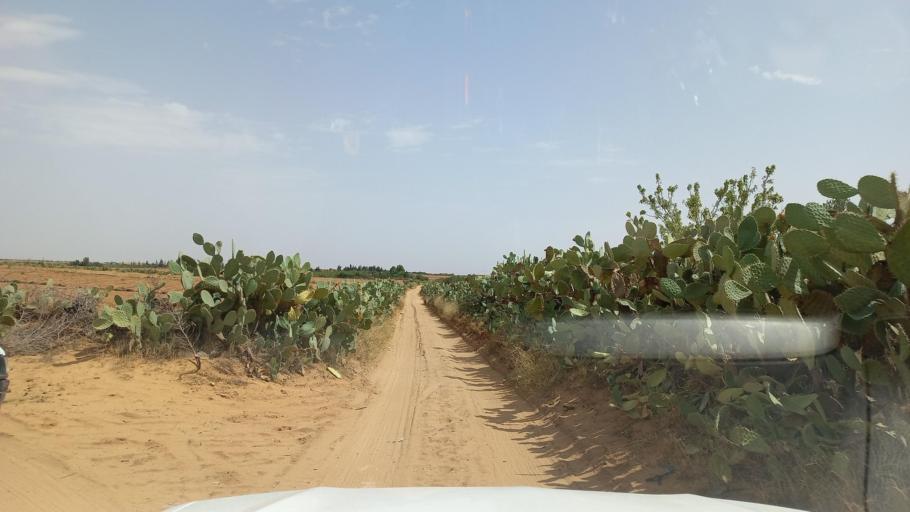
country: TN
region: Al Qasrayn
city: Kasserine
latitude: 35.2530
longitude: 9.0575
